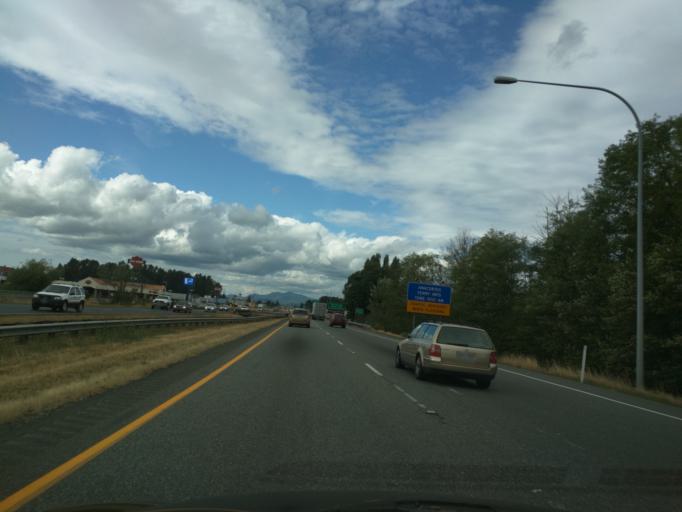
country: US
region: Washington
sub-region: Skagit County
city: Burlington
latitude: 48.4579
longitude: -122.3414
